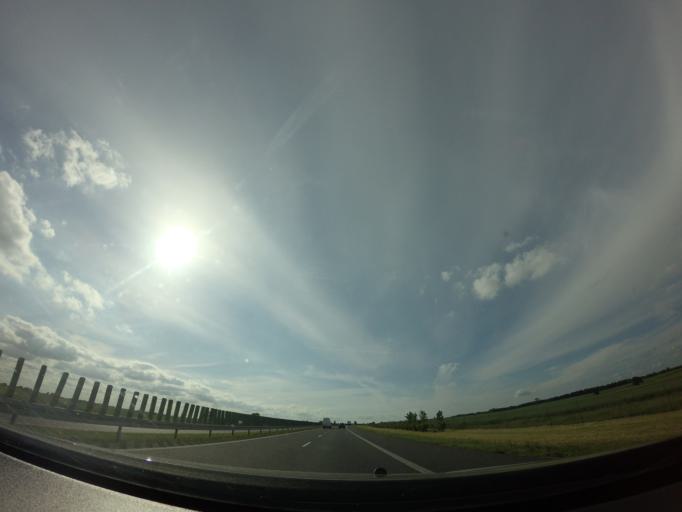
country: PL
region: West Pomeranian Voivodeship
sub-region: Powiat pyrzycki
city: Warnice
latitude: 53.3170
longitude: 14.9762
